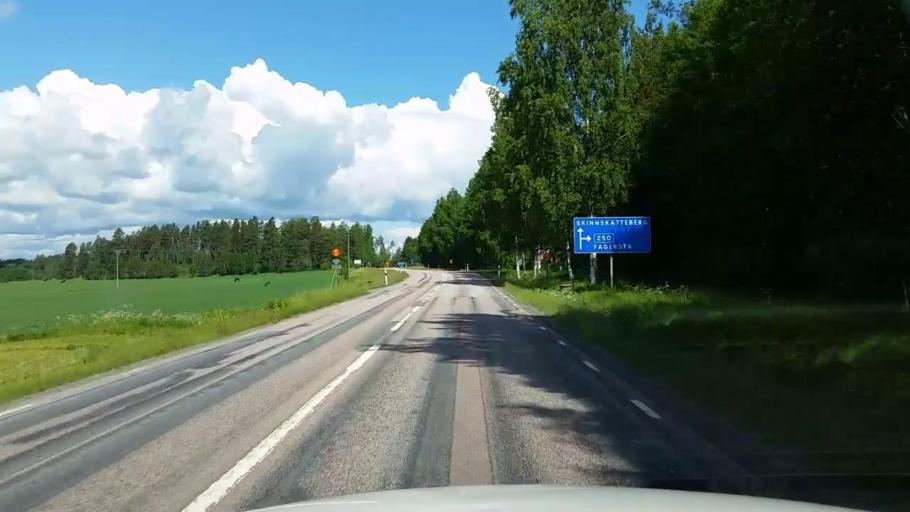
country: SE
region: Vaestmanland
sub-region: Kopings Kommun
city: Kolsva
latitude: 59.6784
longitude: 15.7650
